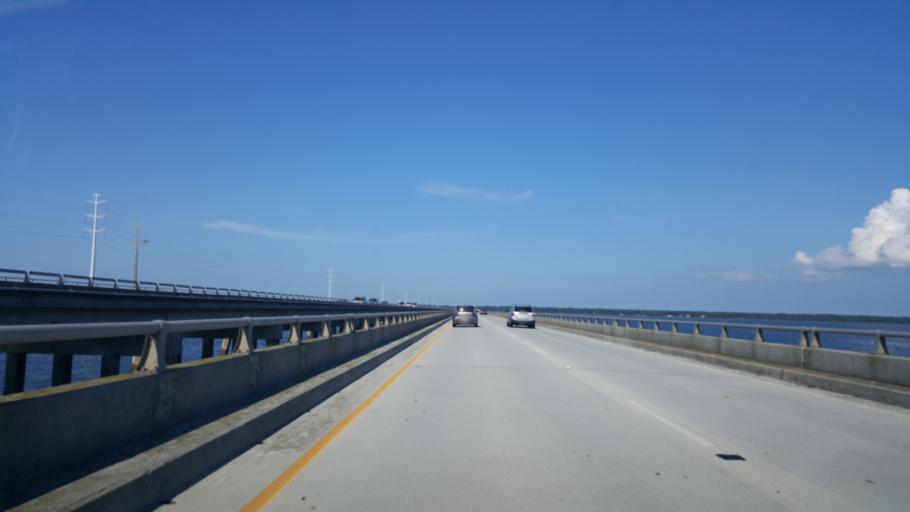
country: US
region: North Carolina
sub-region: Dare County
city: Southern Shores
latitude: 36.0847
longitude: -75.7741
